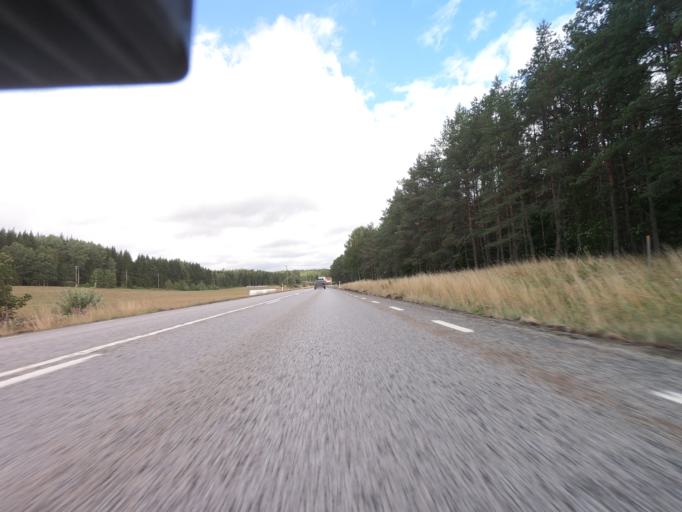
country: SE
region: Joenkoeping
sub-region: Vaggeryds Kommun
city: Vaggeryd
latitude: 57.5353
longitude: 14.2703
